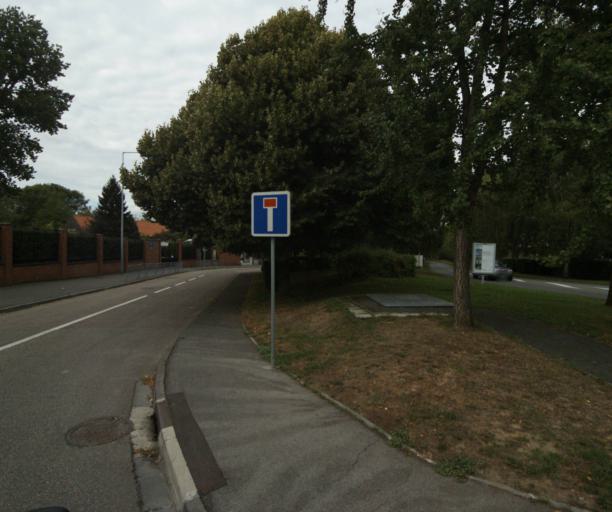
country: FR
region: Nord-Pas-de-Calais
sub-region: Departement du Nord
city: Mons-en-Baroeul
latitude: 50.6474
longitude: 3.1107
